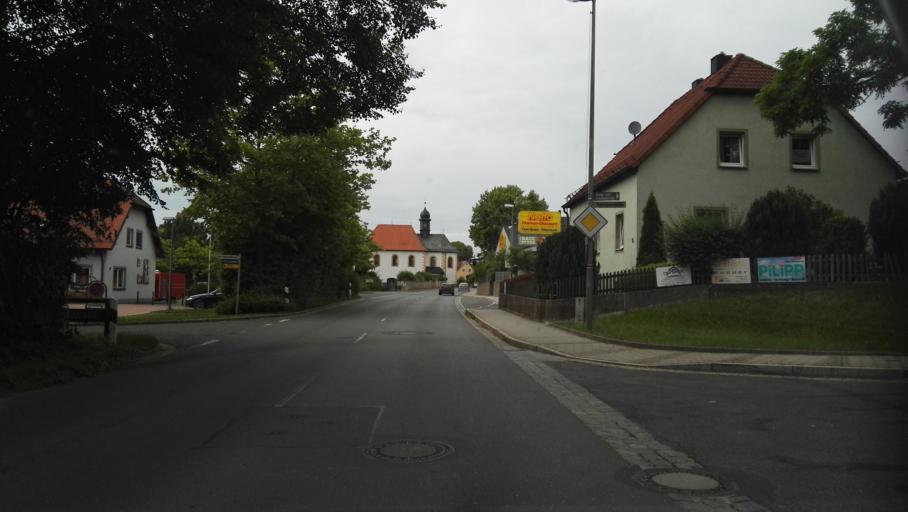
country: DE
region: Bavaria
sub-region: Upper Franconia
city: Hollfeld
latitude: 49.9332
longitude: 11.2956
